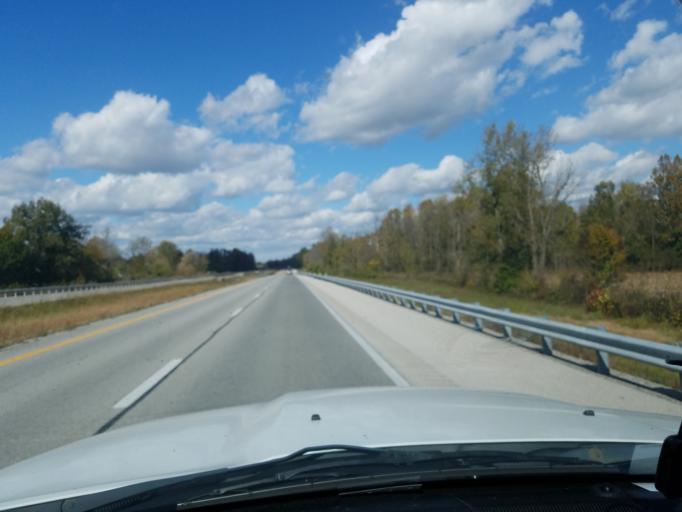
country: US
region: Kentucky
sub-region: Daviess County
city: Masonville
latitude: 37.6443
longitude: -86.9979
